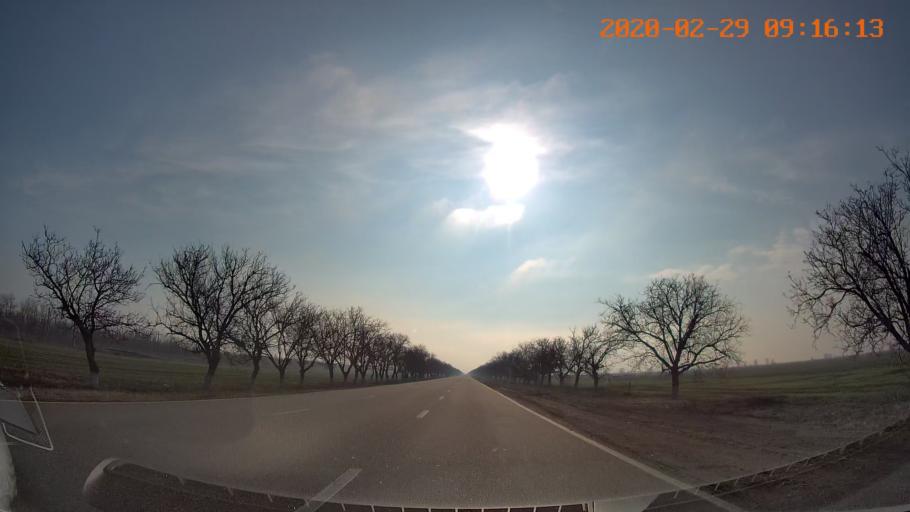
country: MD
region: Telenesti
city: Pervomaisc
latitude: 46.7938
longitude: 29.8825
